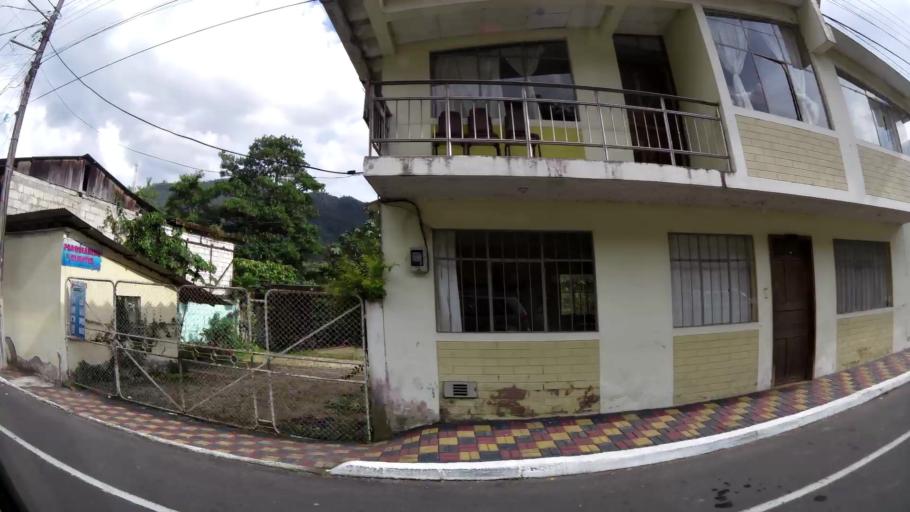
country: EC
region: Tungurahua
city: Banos
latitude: -1.4131
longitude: -78.2090
